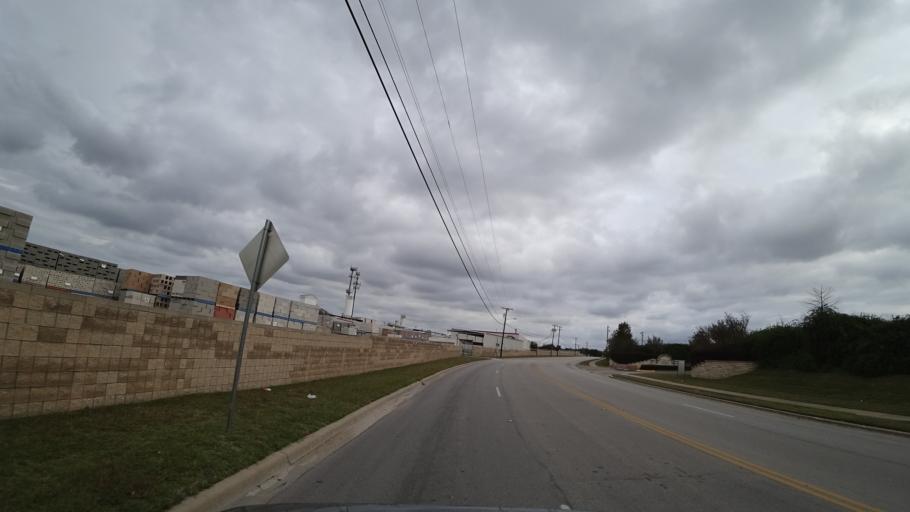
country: US
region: Texas
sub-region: Williamson County
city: Round Rock
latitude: 30.5028
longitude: -97.6871
